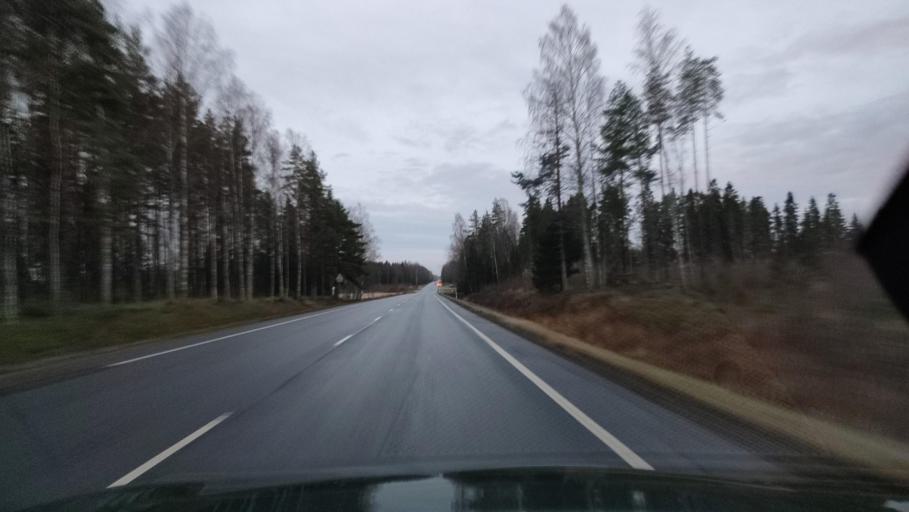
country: FI
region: Ostrobothnia
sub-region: Vaasa
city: Ristinummi
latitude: 63.0097
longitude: 21.7621
